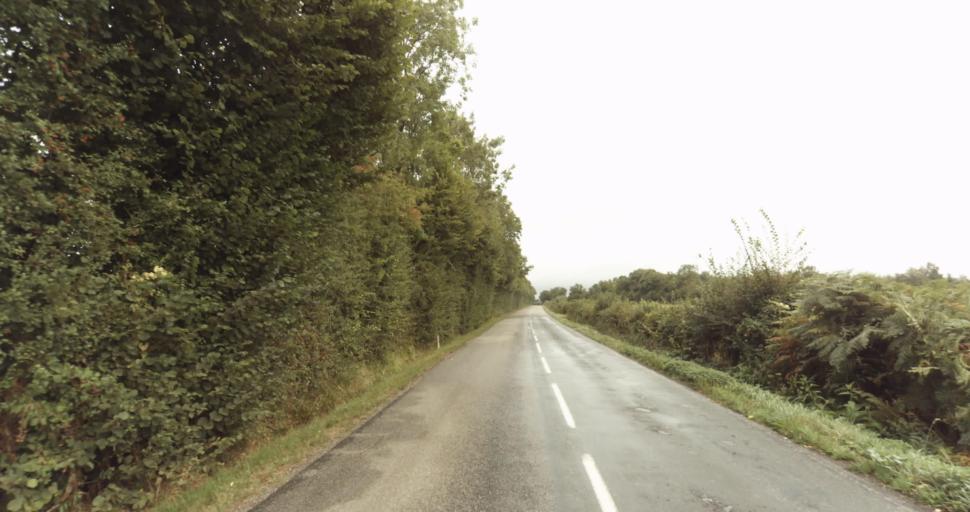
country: FR
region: Lower Normandy
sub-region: Departement de l'Orne
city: Vimoutiers
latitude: 48.8716
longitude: 0.1873
